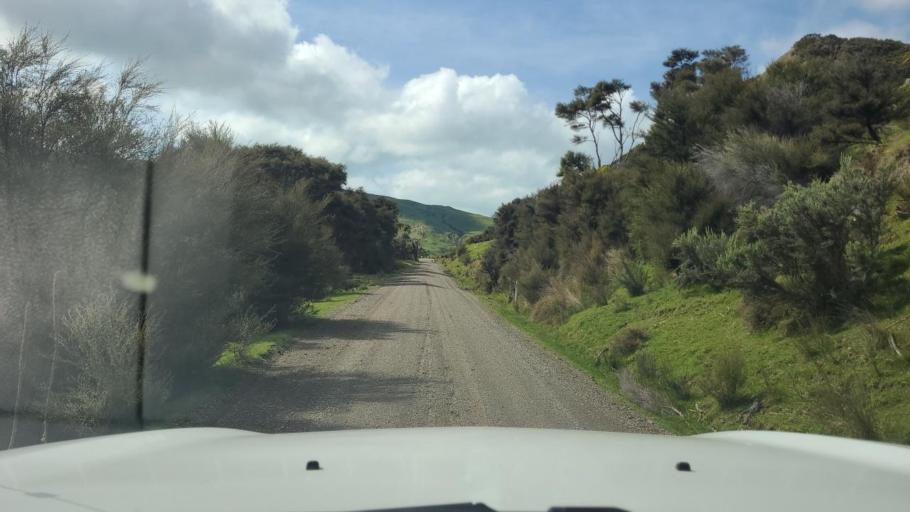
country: NZ
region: Wellington
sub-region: South Wairarapa District
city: Waipawa
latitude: -41.3736
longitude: 175.7163
